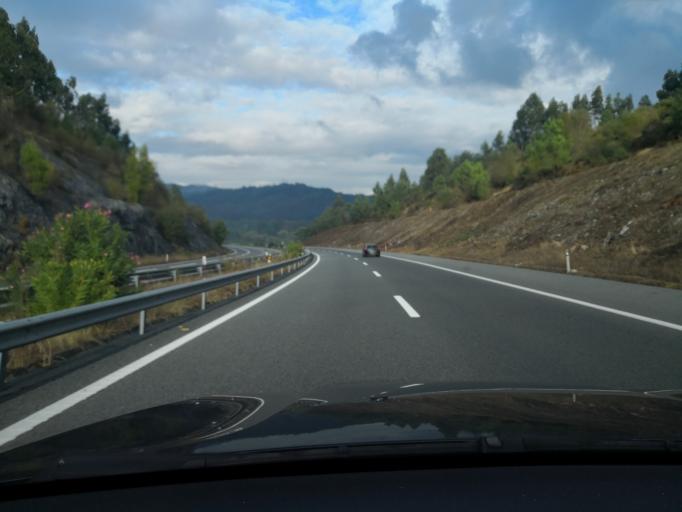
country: PT
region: Braga
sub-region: Guimaraes
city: Serzedo
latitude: 41.3984
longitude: -8.2351
